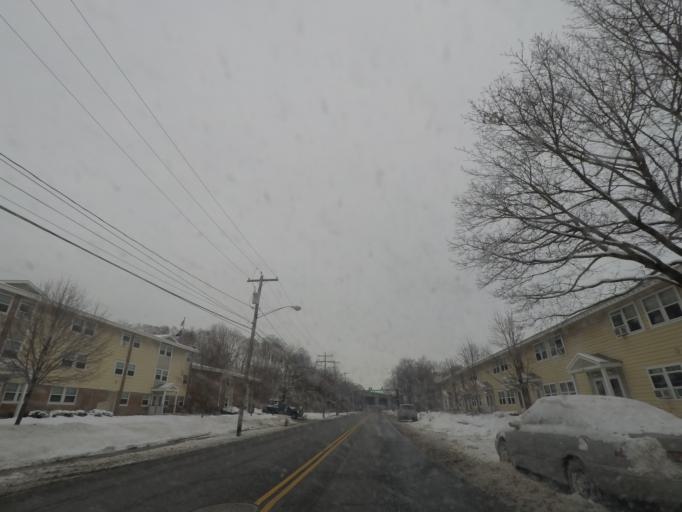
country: US
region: New York
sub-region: Albany County
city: Albany
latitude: 42.6313
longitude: -73.7651
